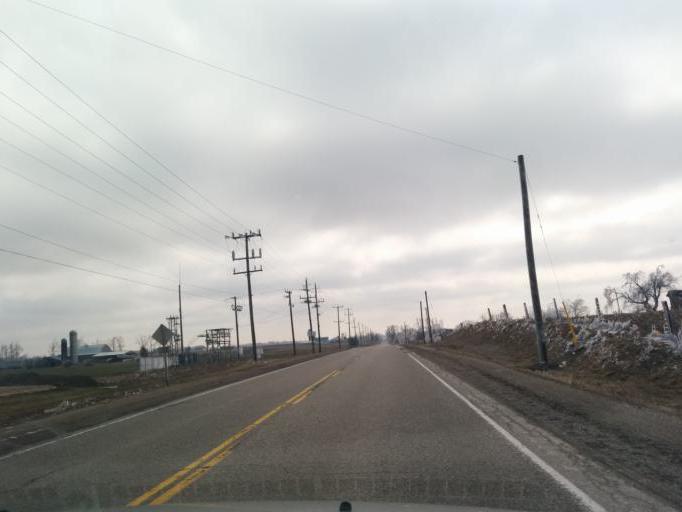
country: CA
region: Ontario
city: Waterloo
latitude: 43.6322
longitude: -80.5501
